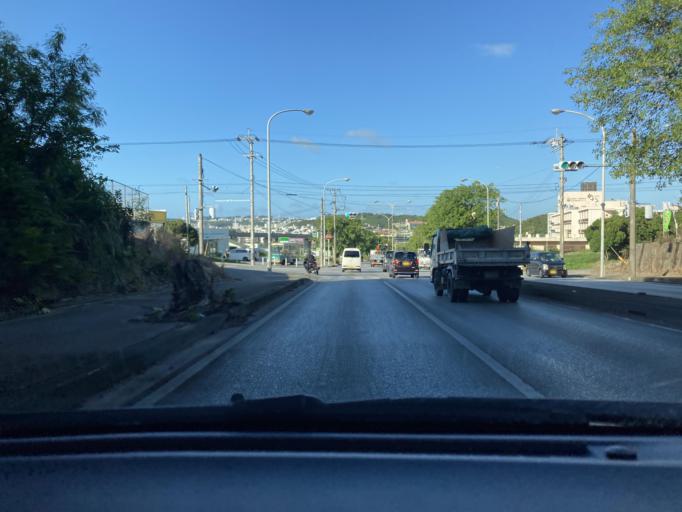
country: JP
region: Okinawa
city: Tomigusuku
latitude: 26.1761
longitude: 127.7130
